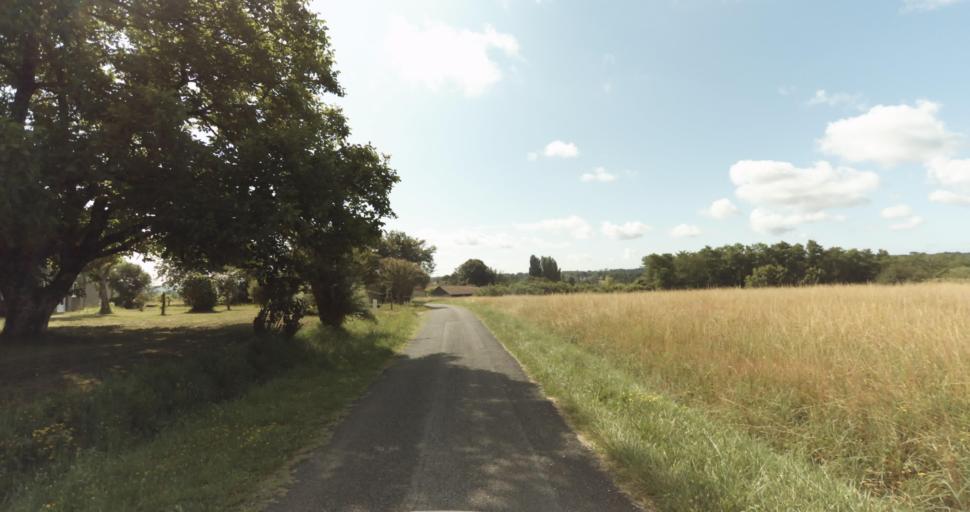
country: FR
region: Aquitaine
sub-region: Departement de la Gironde
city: Bazas
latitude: 44.4370
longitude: -0.1997
